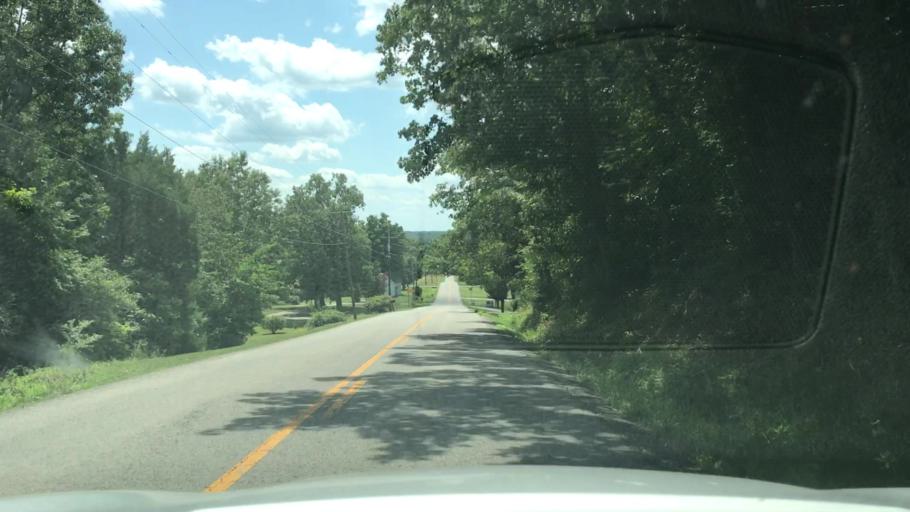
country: US
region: Kentucky
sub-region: Muhlenberg County
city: Greenville
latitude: 37.1634
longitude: -87.2497
